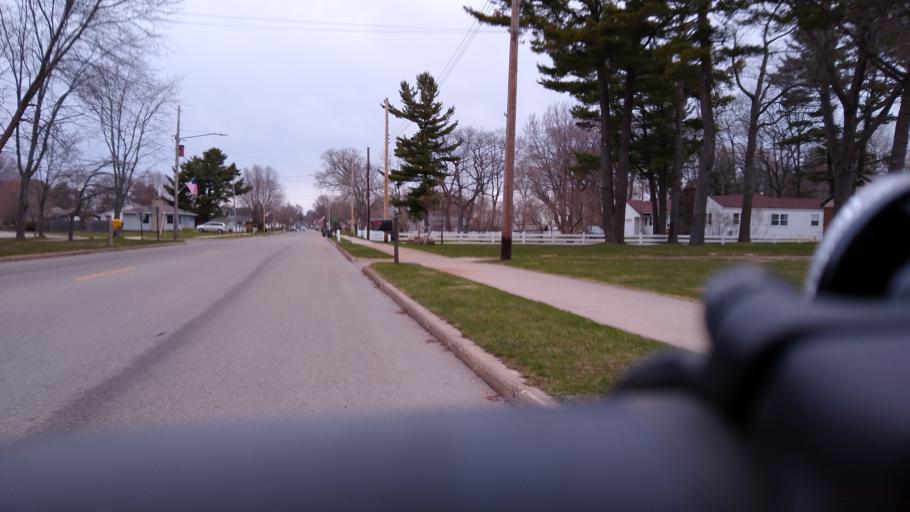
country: US
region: Michigan
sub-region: Delta County
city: Escanaba
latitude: 45.7281
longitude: -87.0657
